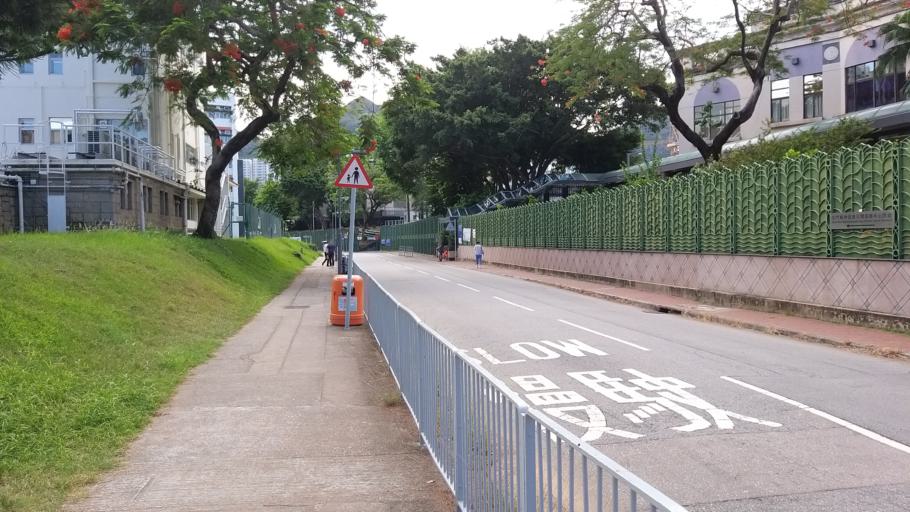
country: HK
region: Tuen Mun
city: Tuen Mun
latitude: 22.4084
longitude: 113.9733
